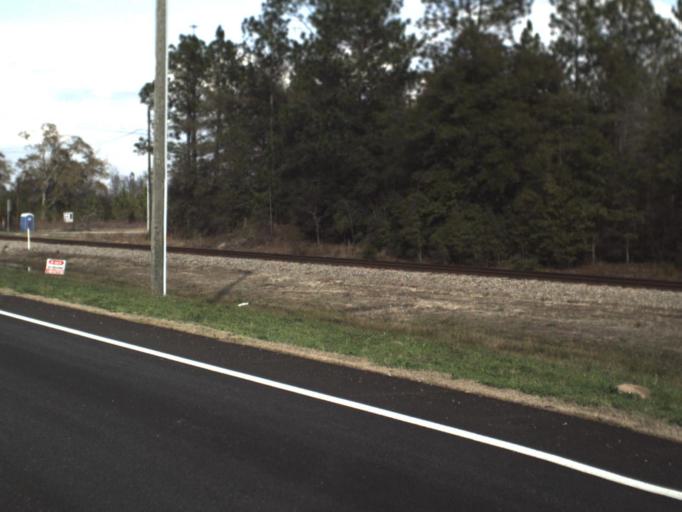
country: US
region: Florida
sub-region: Bay County
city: Youngstown
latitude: 30.4348
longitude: -85.4273
